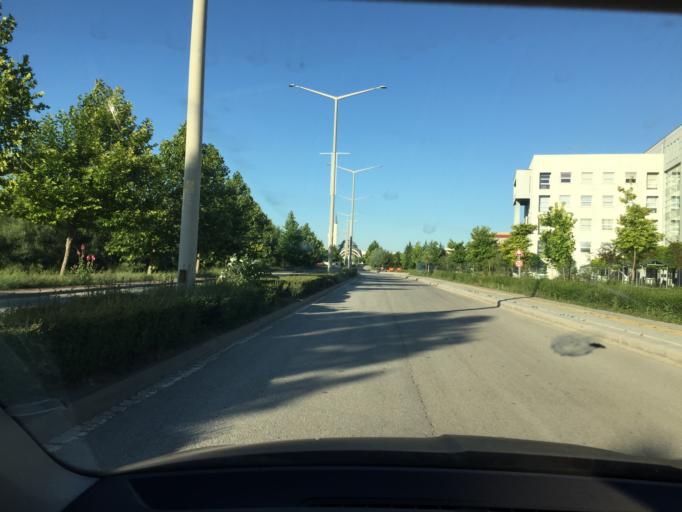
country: TR
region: Eskisehir
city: Eskisehir
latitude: 39.7520
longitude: 30.4786
